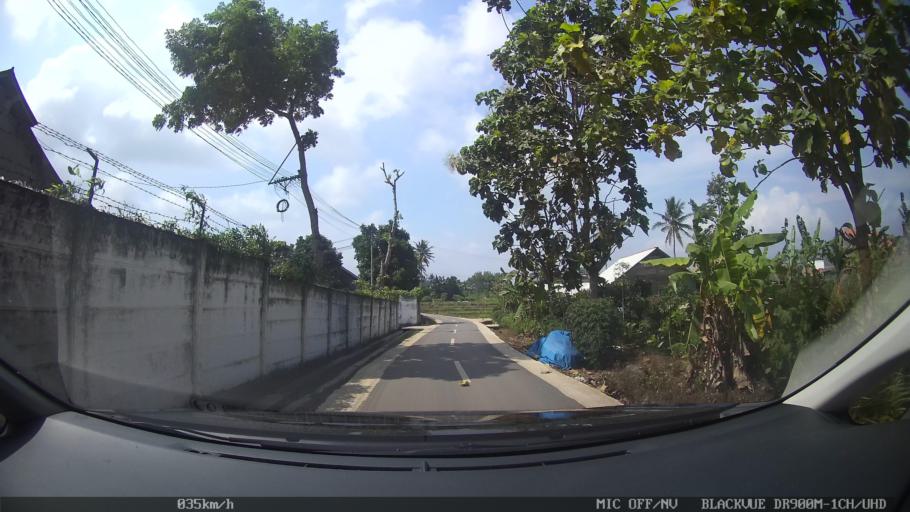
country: ID
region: Lampung
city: Kedaton
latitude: -5.3343
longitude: 105.2729
